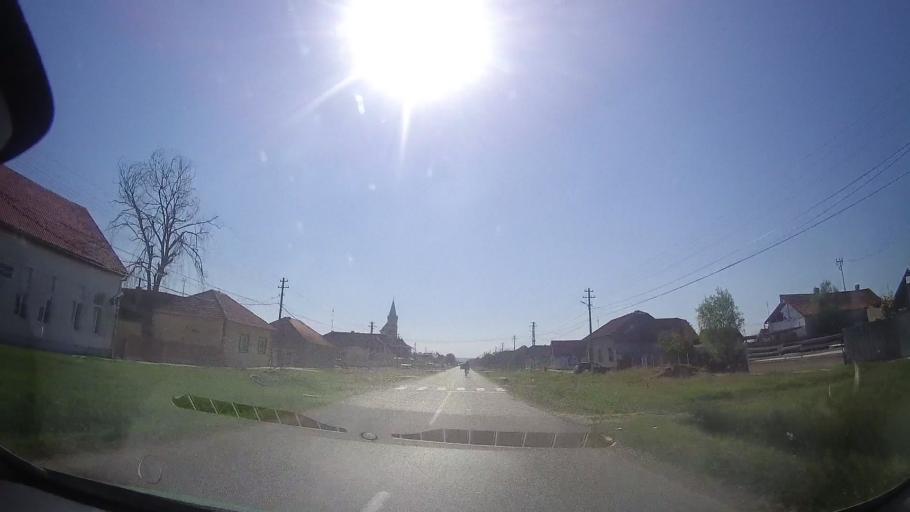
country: RO
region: Timis
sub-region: Comuna Bethausen
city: Bethausen
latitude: 45.8390
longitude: 21.9595
